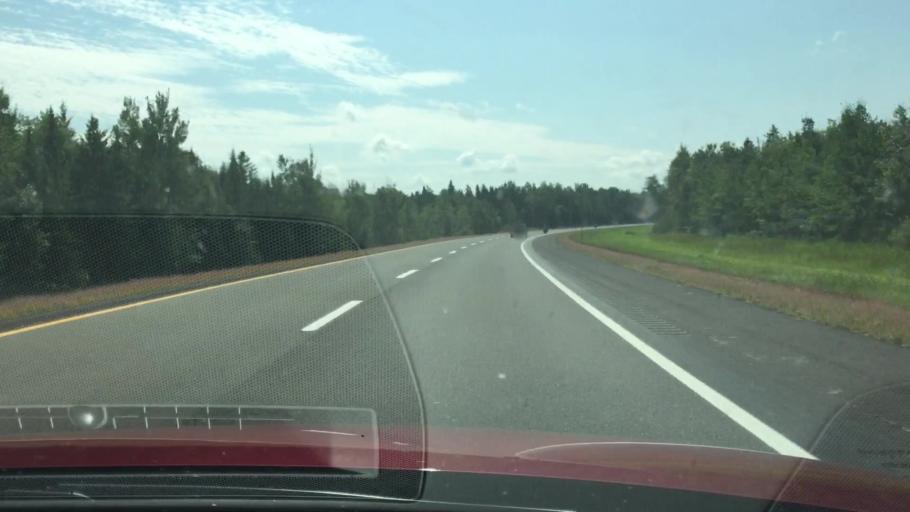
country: US
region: Maine
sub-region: Penobscot County
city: Patten
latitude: 45.9937
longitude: -68.2798
